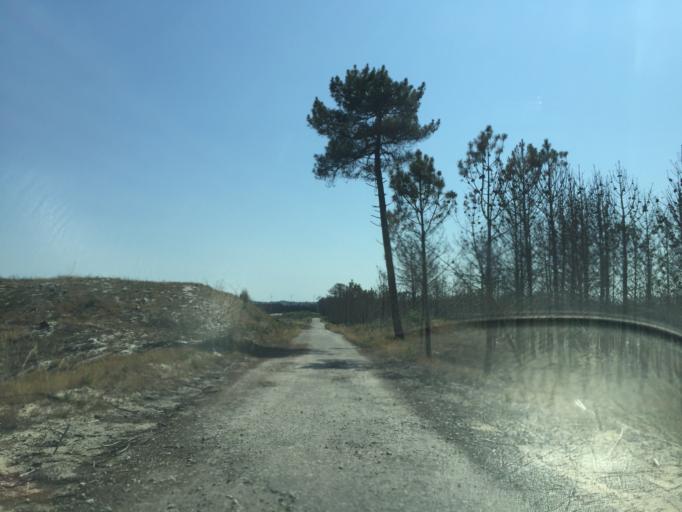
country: PT
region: Coimbra
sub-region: Figueira da Foz
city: Alhadas
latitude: 40.2612
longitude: -8.8343
